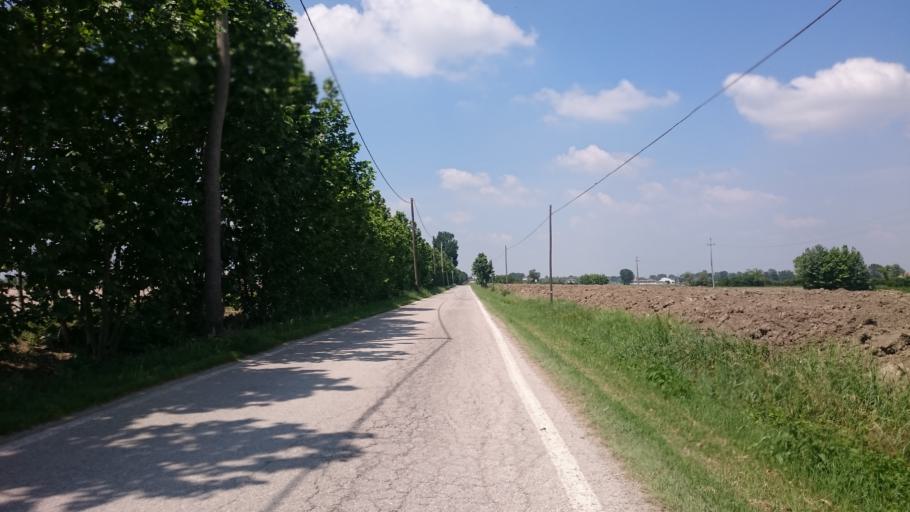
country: IT
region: Lombardy
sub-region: Provincia di Mantova
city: Bagnolo San Vito
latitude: 45.0935
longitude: 10.9113
